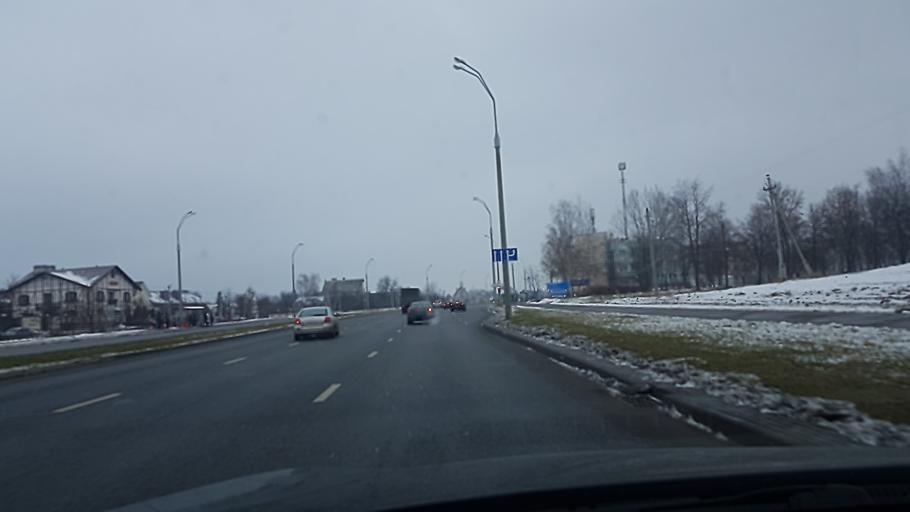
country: BY
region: Minsk
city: Minsk
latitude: 53.9515
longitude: 27.5354
